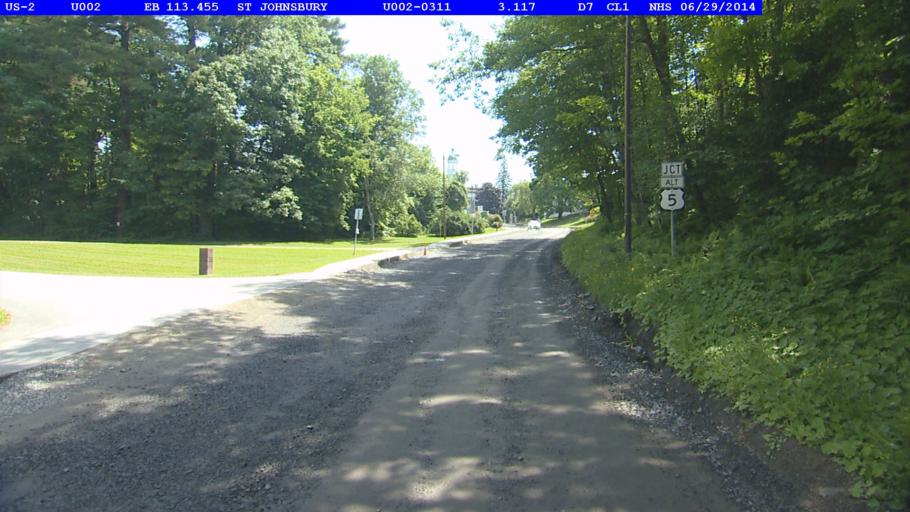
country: US
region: Vermont
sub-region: Caledonia County
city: Saint Johnsbury
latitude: 44.4165
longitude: -72.0221
